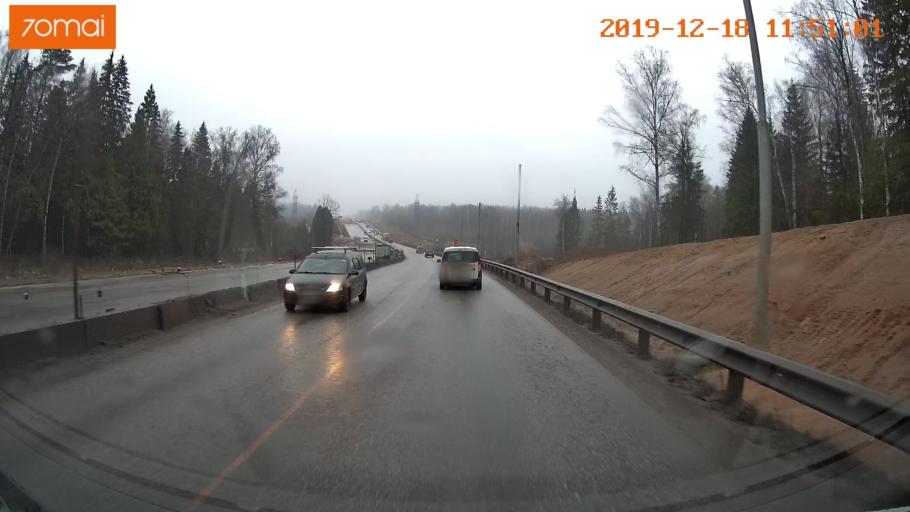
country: RU
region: Moskovskaya
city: Yershovo
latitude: 55.7904
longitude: 36.9217
